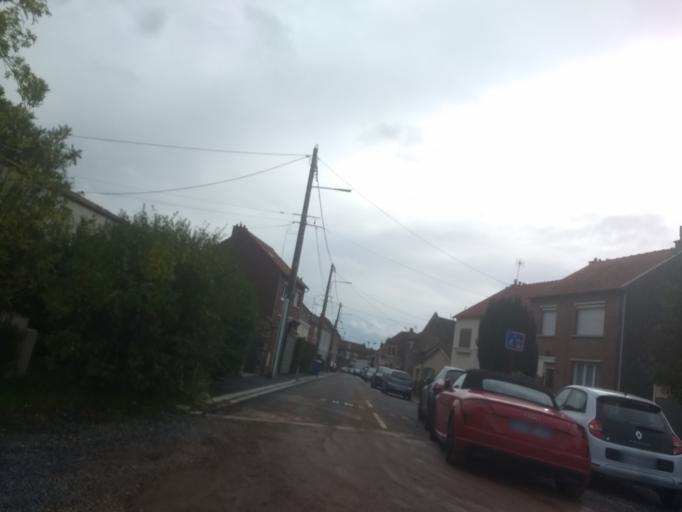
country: FR
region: Nord-Pas-de-Calais
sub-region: Departement du Pas-de-Calais
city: Saint-Nicolas
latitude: 50.3020
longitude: 2.7732
